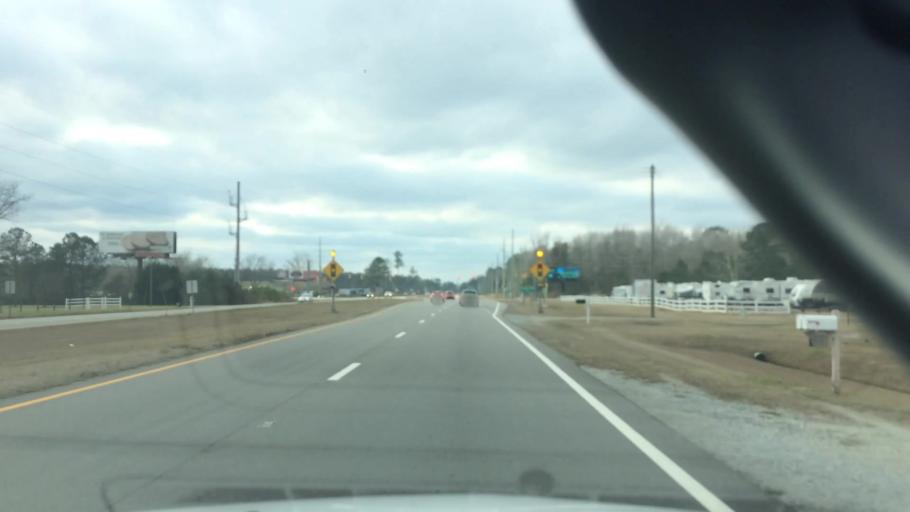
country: US
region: North Carolina
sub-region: Brunswick County
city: Carolina Shores
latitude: 33.9390
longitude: -78.5529
